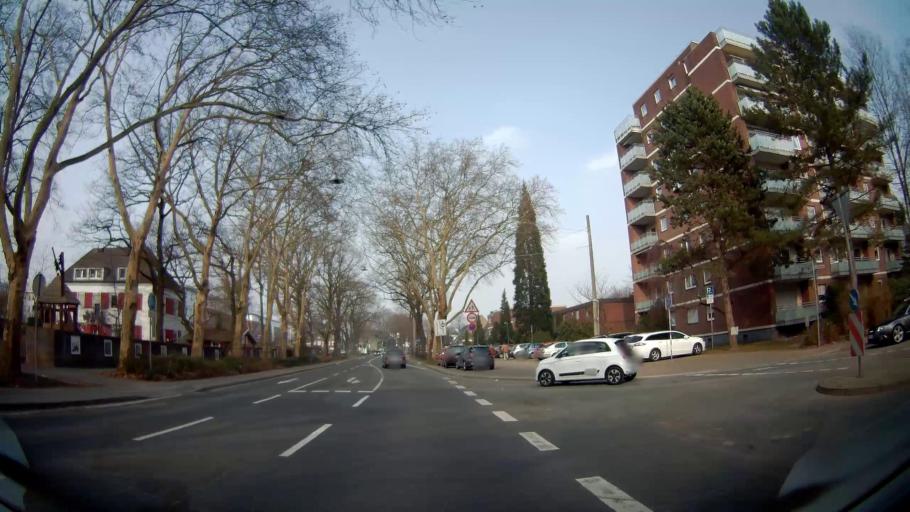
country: DE
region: North Rhine-Westphalia
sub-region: Regierungsbezirk Munster
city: Bottrop
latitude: 51.5132
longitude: 6.9083
